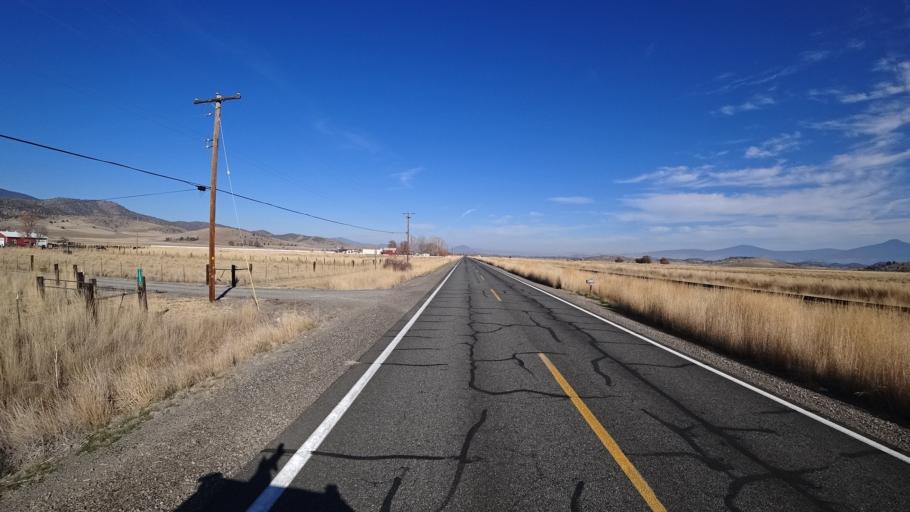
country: US
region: California
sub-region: Siskiyou County
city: Montague
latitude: 41.5909
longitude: -122.5241
